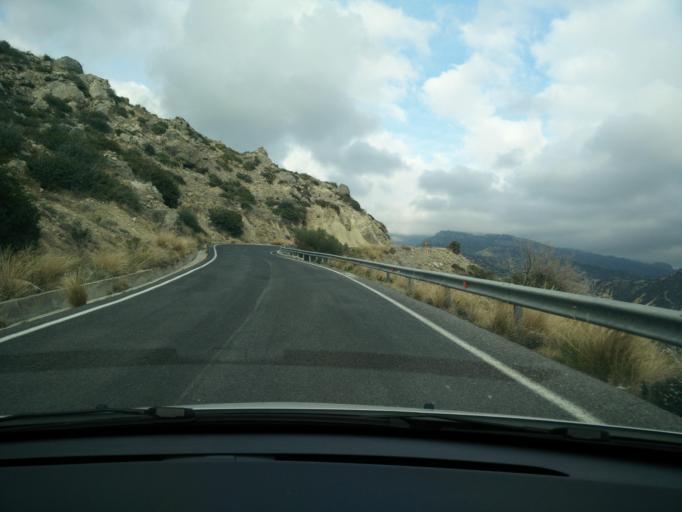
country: GR
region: Crete
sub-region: Nomos Lasithiou
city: Gra Liyia
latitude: 35.0157
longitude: 25.5778
